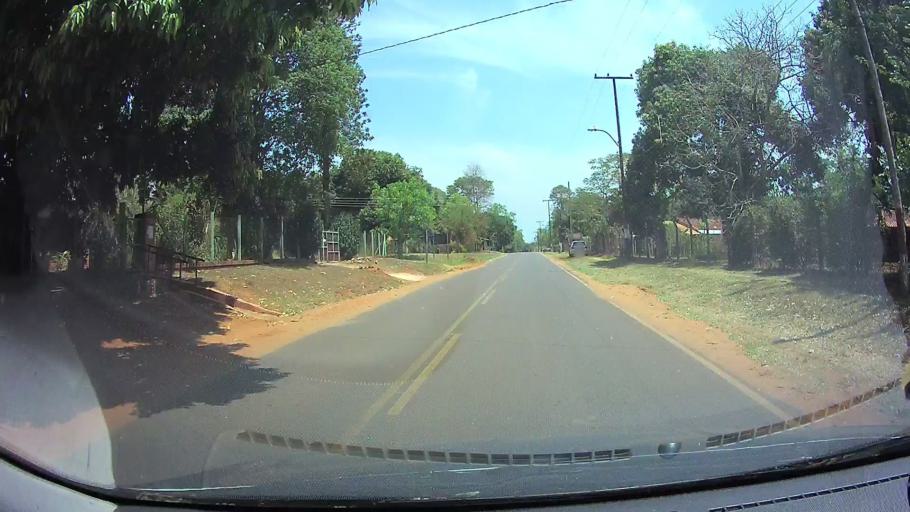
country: PY
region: Central
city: Ita
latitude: -25.4356
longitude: -57.3976
